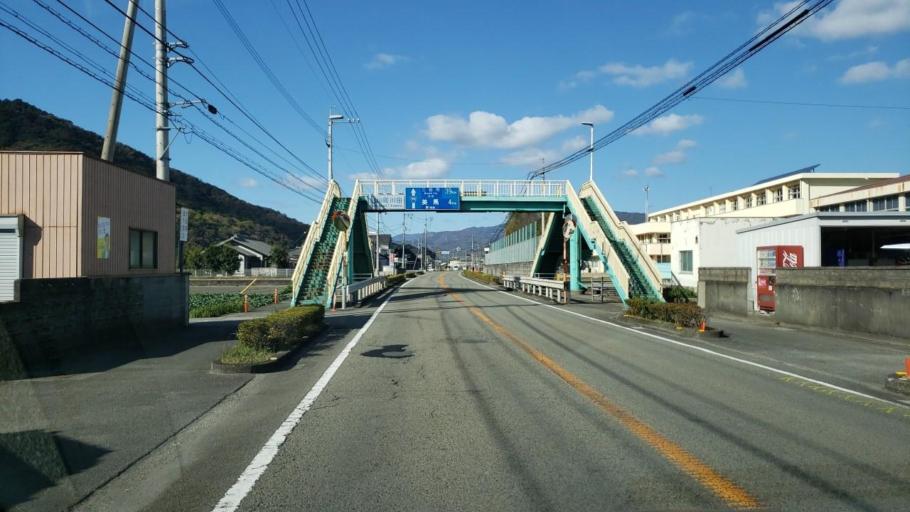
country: JP
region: Tokushima
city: Wakimachi
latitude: 34.0609
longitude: 134.2098
